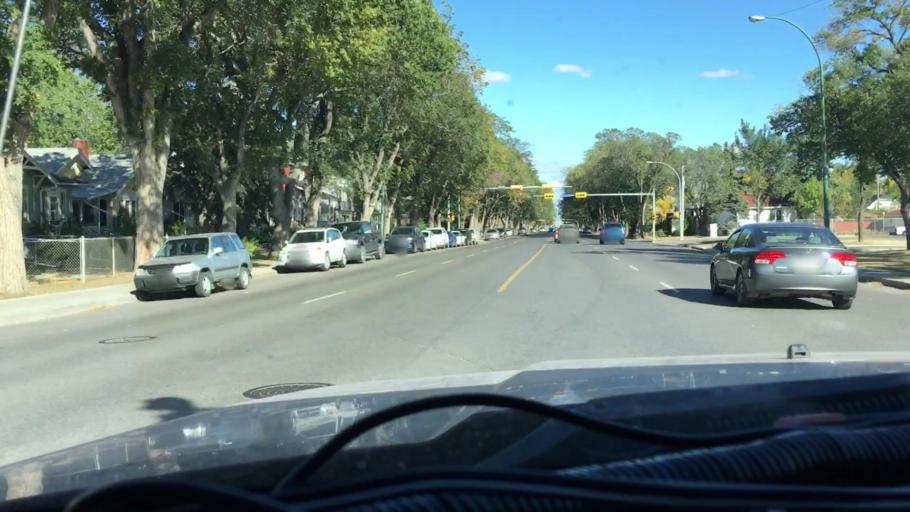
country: CA
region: Saskatchewan
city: Regina
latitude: 50.4551
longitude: -104.6370
